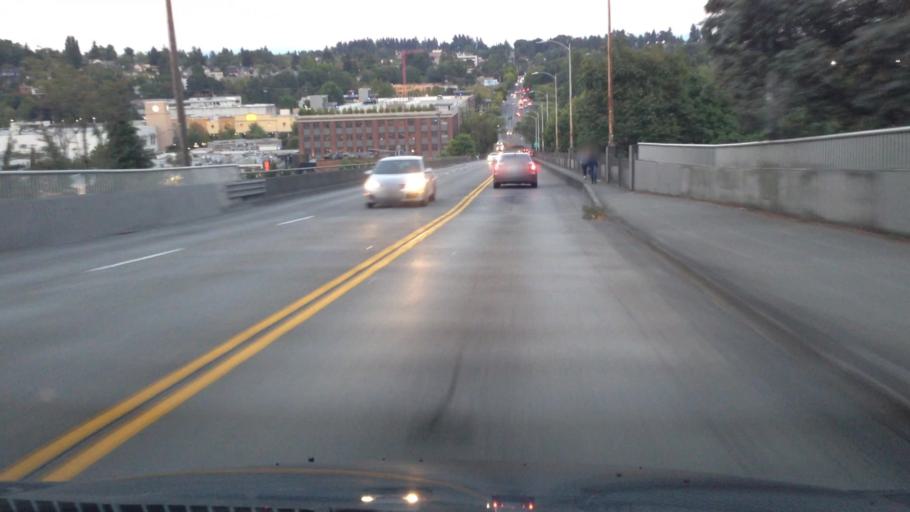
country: US
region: Washington
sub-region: King County
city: Seattle
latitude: 47.6613
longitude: -122.3028
